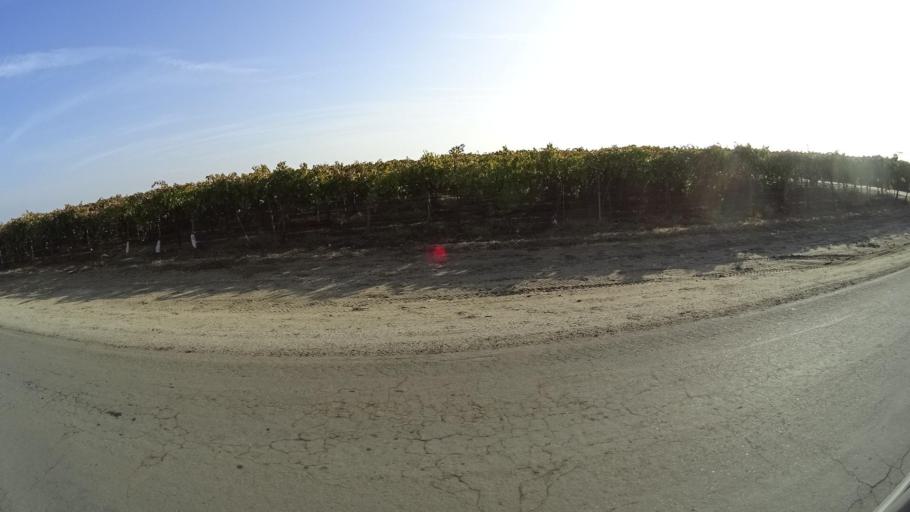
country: US
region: California
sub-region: Kern County
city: McFarland
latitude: 35.6967
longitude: -119.1871
